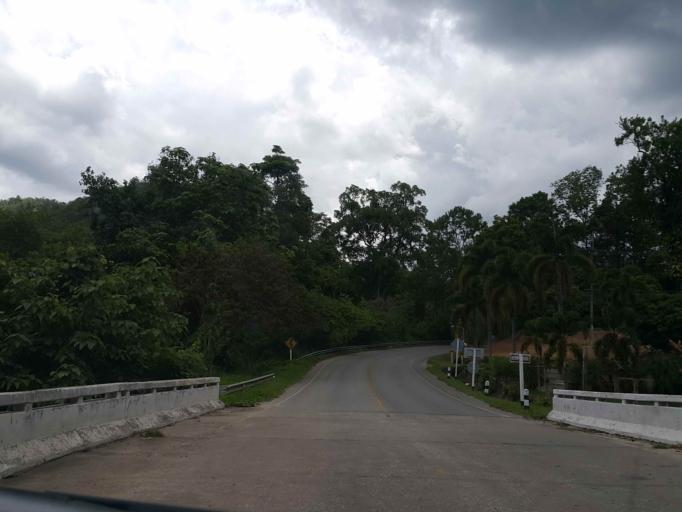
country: TH
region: Chiang Mai
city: Hang Dong
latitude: 18.7795
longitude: 98.8528
